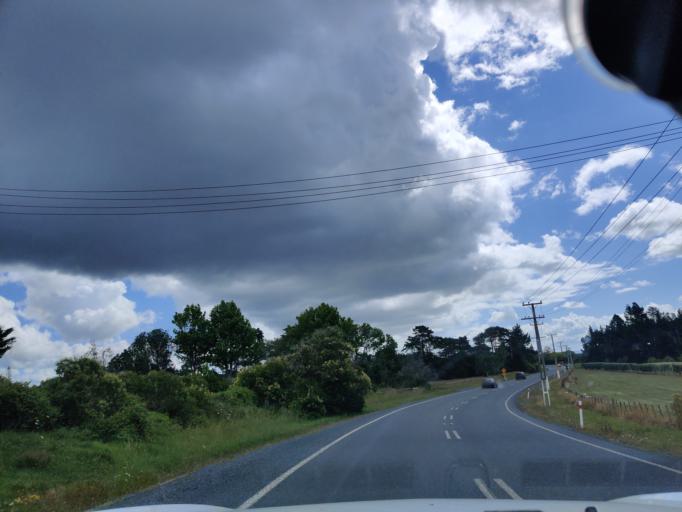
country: NZ
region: Auckland
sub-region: Auckland
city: Red Hill
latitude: -37.0415
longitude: 174.9838
